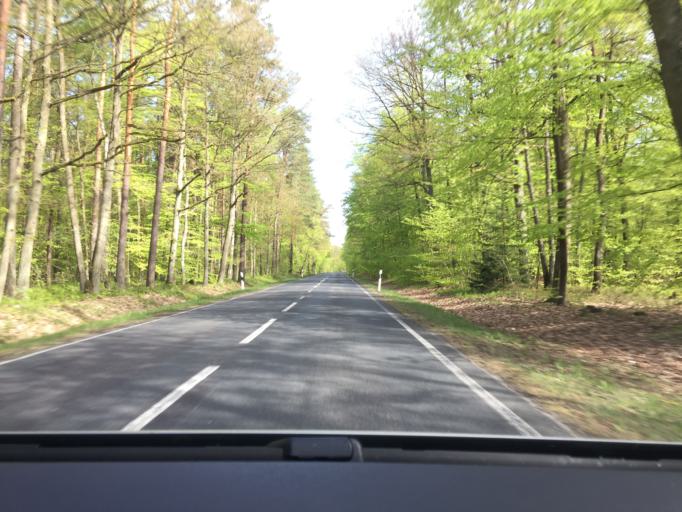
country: DE
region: Mecklenburg-Vorpommern
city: Torgelow
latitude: 53.6640
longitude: 14.0222
